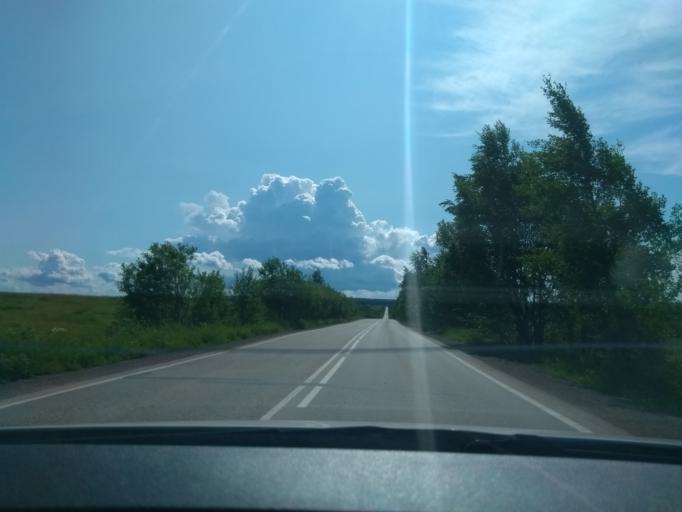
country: RU
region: Perm
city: Bershet'
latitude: 57.8238
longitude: 56.4256
